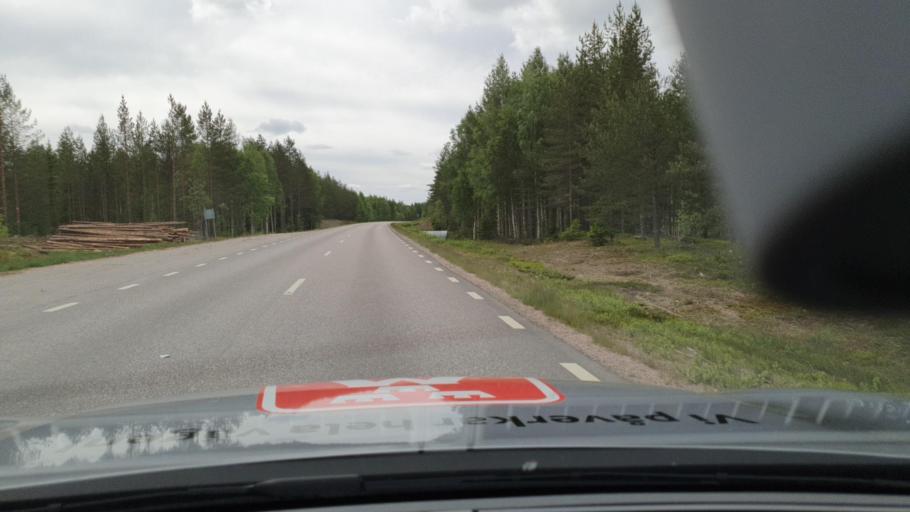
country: SE
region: Norrbotten
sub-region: Kalix Kommun
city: Kalix
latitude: 65.8591
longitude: 23.4792
